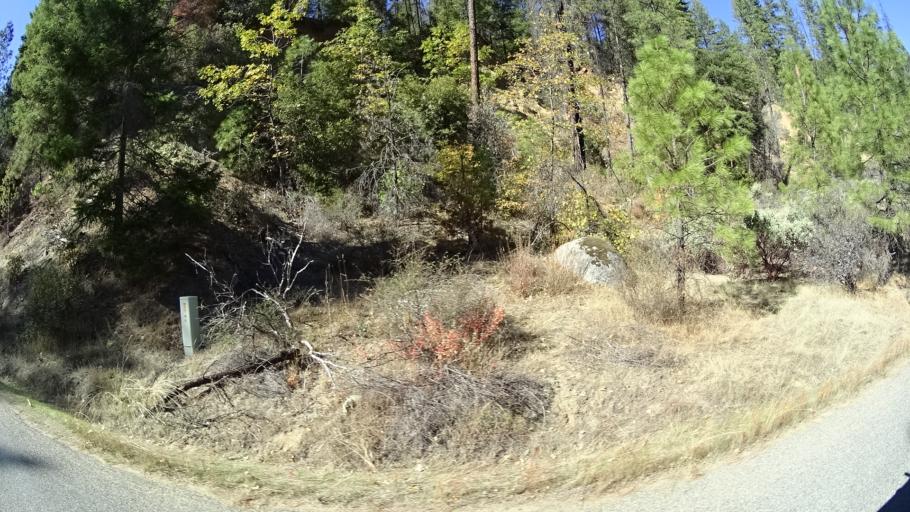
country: US
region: California
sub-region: Siskiyou County
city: Happy Camp
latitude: 41.3038
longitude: -123.2120
